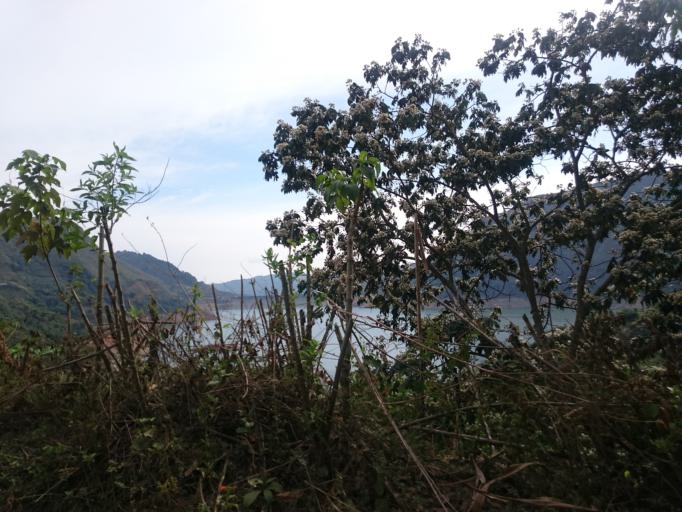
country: CO
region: Cauca
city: Suarez
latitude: 2.9309
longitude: -76.7184
